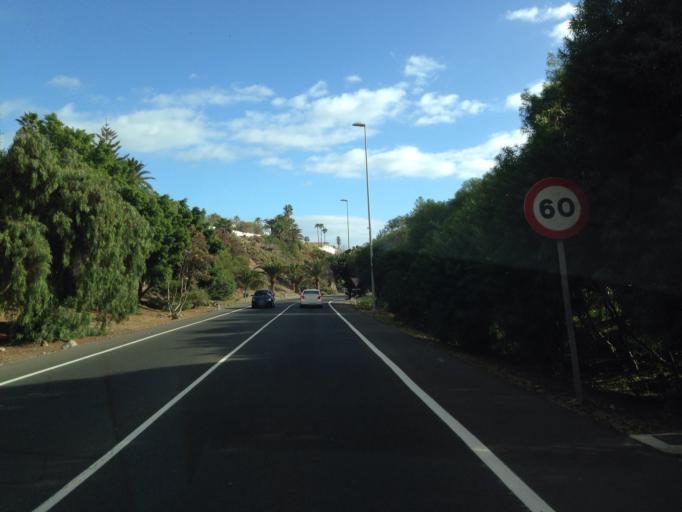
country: ES
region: Canary Islands
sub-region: Provincia de Las Palmas
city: Maspalomas
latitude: 27.7627
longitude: -15.5865
